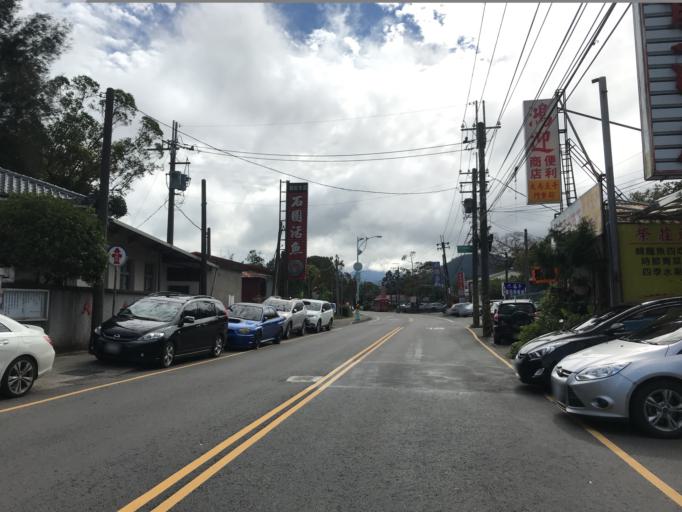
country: TW
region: Taiwan
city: Daxi
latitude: 24.8394
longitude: 121.2404
